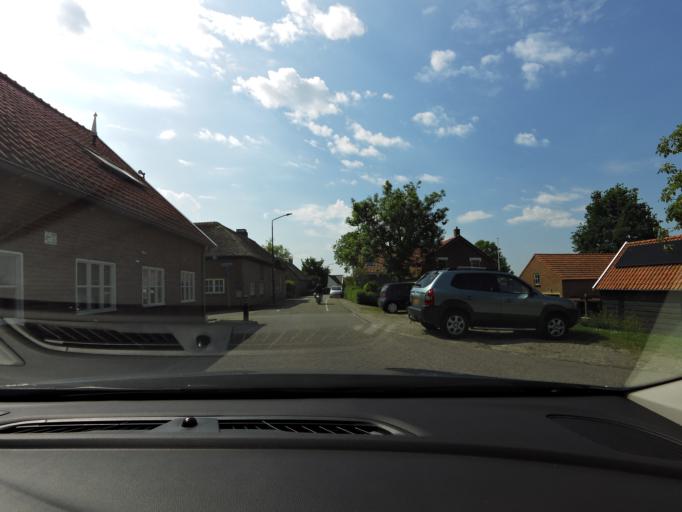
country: NL
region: North Brabant
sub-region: Gemeente Woudrichem
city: Almkerk
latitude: 51.7884
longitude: 4.9395
